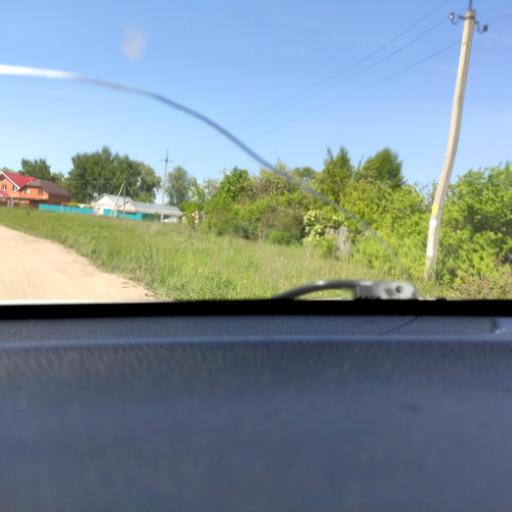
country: RU
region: Tatarstan
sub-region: Gorod Kazan'
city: Kazan
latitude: 55.8634
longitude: 49.1967
